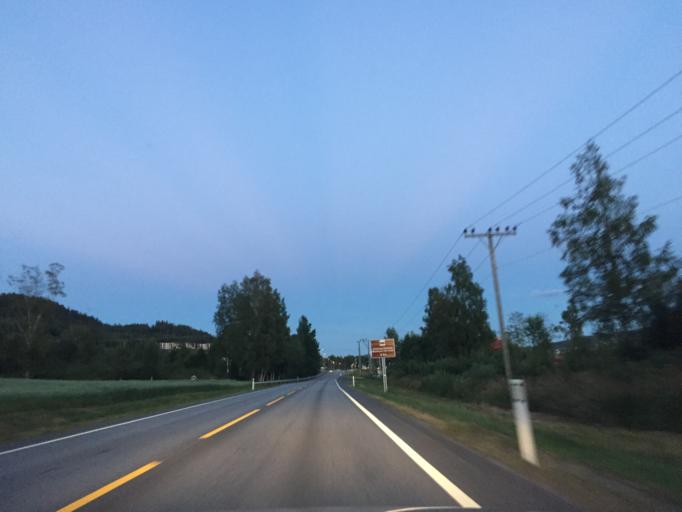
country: NO
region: Hedmark
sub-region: Kongsvinger
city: Kongsvinger
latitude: 60.2106
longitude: 11.9618
